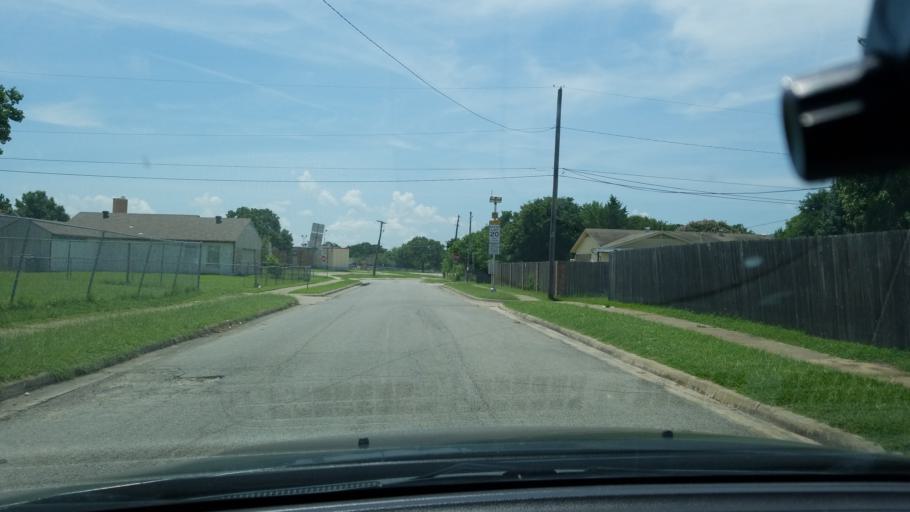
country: US
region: Texas
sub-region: Dallas County
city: Balch Springs
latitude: 32.7424
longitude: -96.6419
